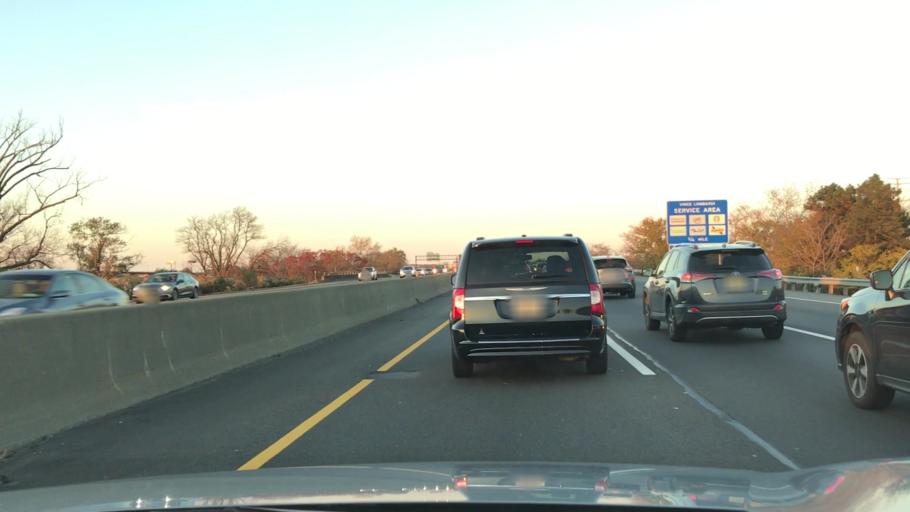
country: US
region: New Jersey
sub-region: Hudson County
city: North Bergen
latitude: 40.8117
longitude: -74.0293
